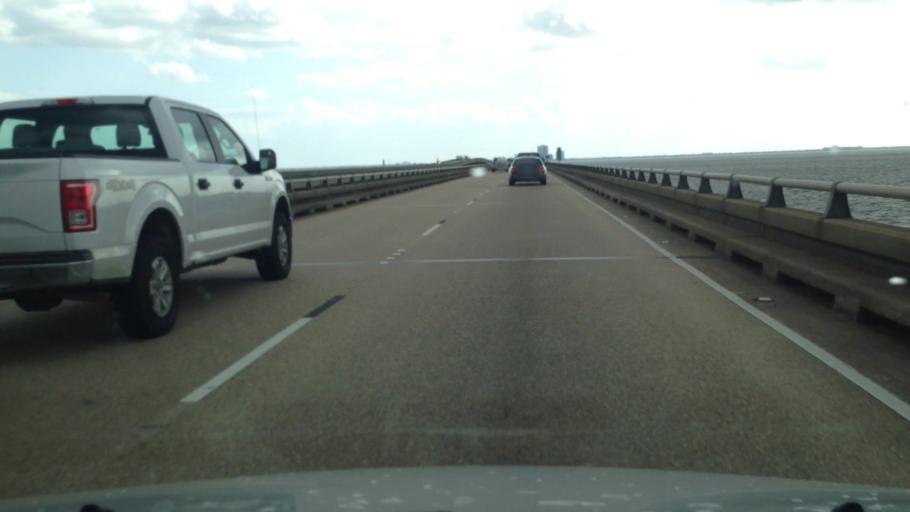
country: US
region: Louisiana
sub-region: Jefferson Parish
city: Metairie
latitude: 30.0832
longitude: -90.1434
